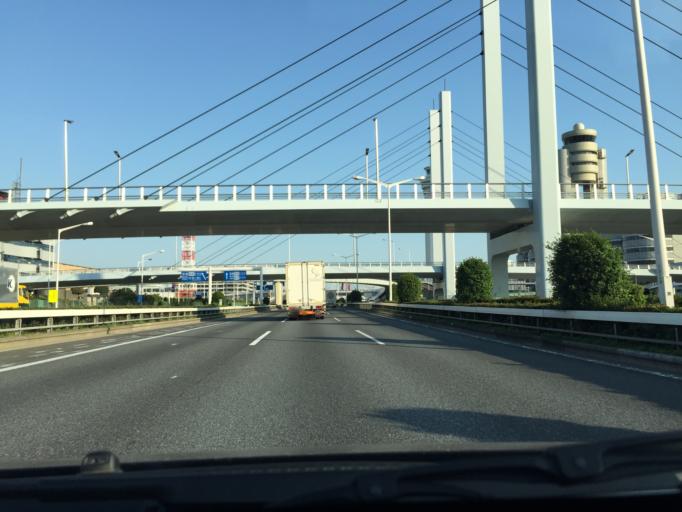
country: JP
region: Kanagawa
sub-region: Kawasaki-shi
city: Kawasaki
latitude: 35.5561
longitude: 139.7822
